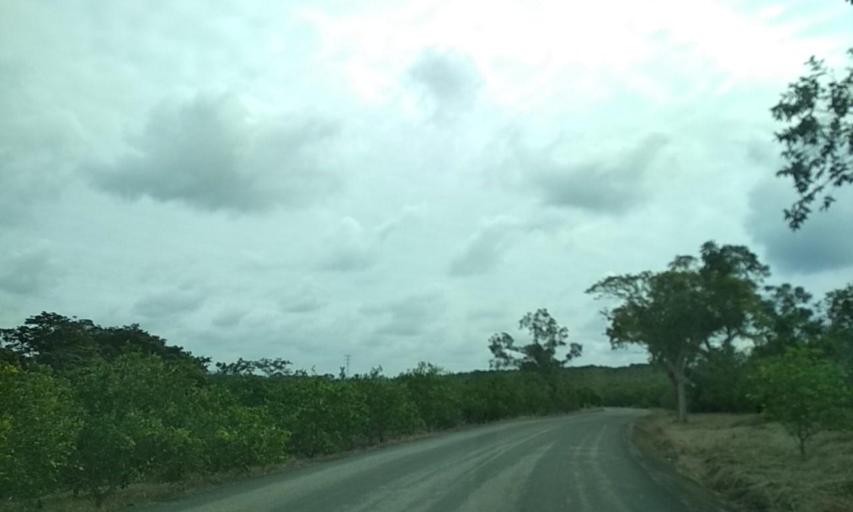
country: MX
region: Veracruz
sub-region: Papantla
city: El Chote
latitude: 20.3545
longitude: -97.3586
